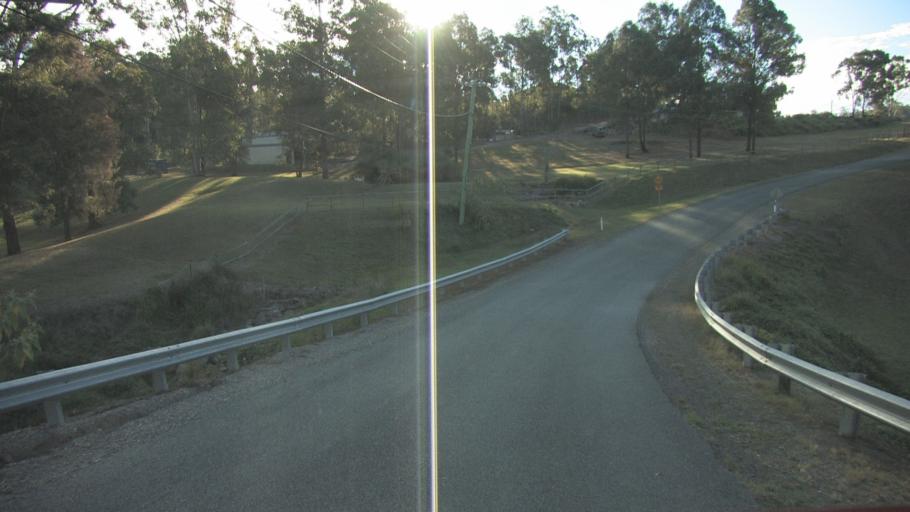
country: AU
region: Queensland
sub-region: Logan
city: Cedar Vale
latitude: -27.9323
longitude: 153.0525
